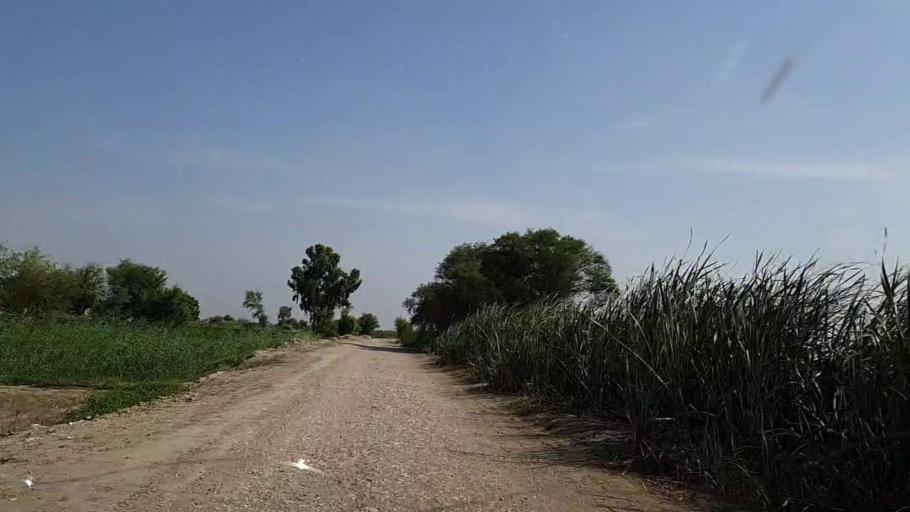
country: PK
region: Sindh
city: Khanpur
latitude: 27.7213
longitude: 69.3607
